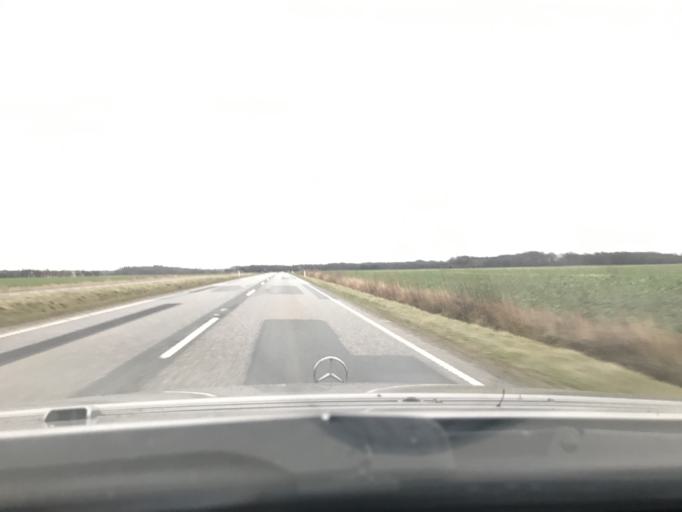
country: DK
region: South Denmark
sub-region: Tonder Kommune
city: Toftlund
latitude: 55.1529
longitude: 9.0995
